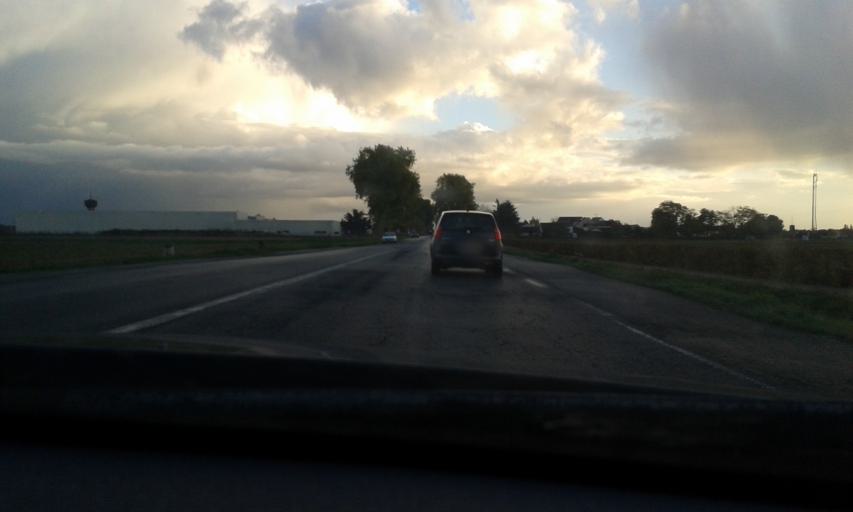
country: FR
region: Centre
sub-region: Departement du Loiret
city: Chevilly
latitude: 48.0392
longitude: 1.8741
